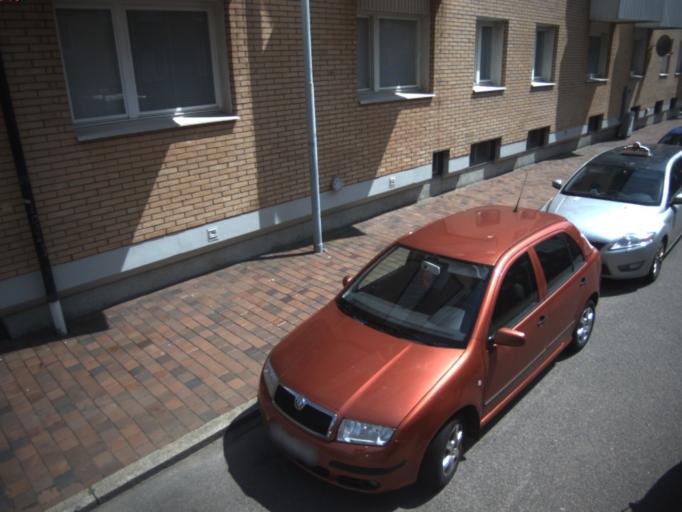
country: SE
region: Skane
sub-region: Helsingborg
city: Helsingborg
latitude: 56.0420
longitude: 12.7128
